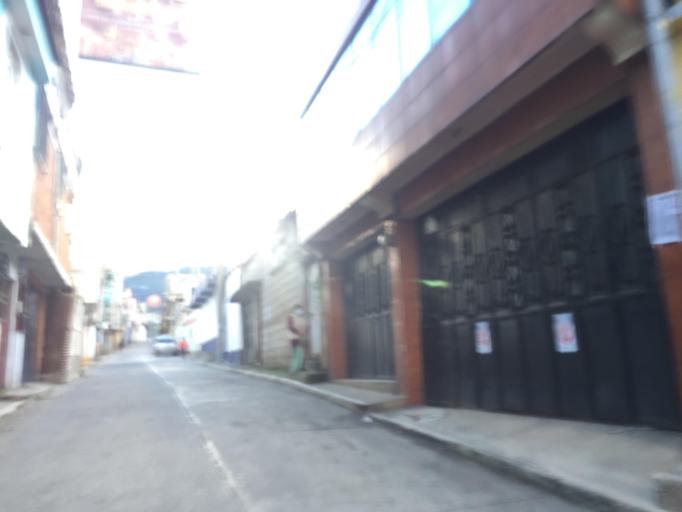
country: GT
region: Totonicapan
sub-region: Municipio de Totonicapan
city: Totonicapan
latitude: 14.9127
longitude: -91.3646
